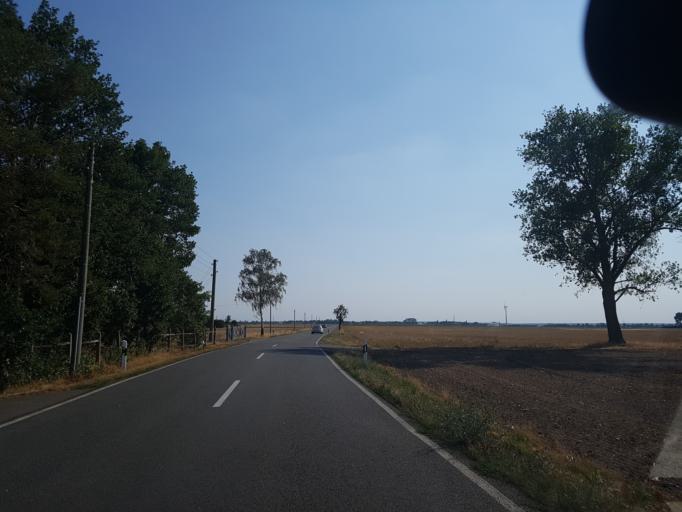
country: DE
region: Saxony-Anhalt
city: Prettin
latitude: 51.6692
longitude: 12.9935
